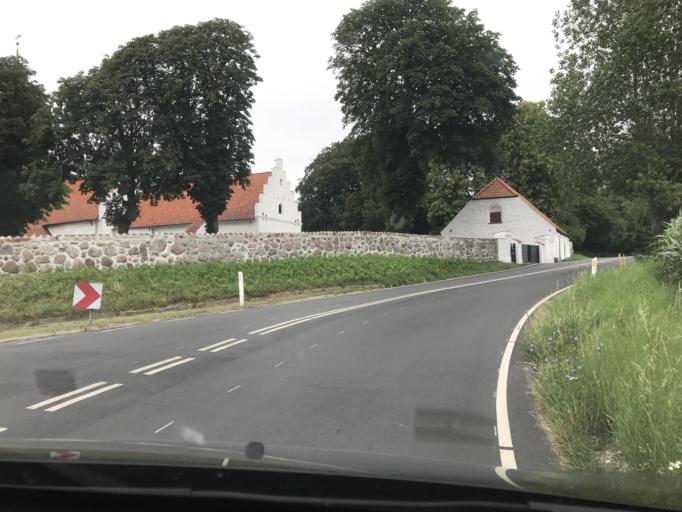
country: DK
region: South Denmark
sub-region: AEro Kommune
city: AEroskobing
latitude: 54.8536
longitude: 10.4004
